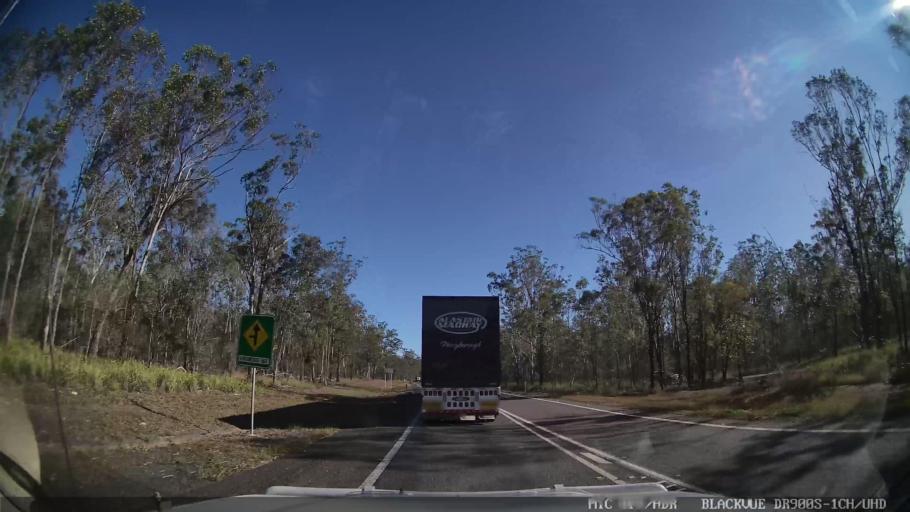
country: AU
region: Queensland
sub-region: Bundaberg
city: Childers
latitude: -25.2118
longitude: 152.0831
